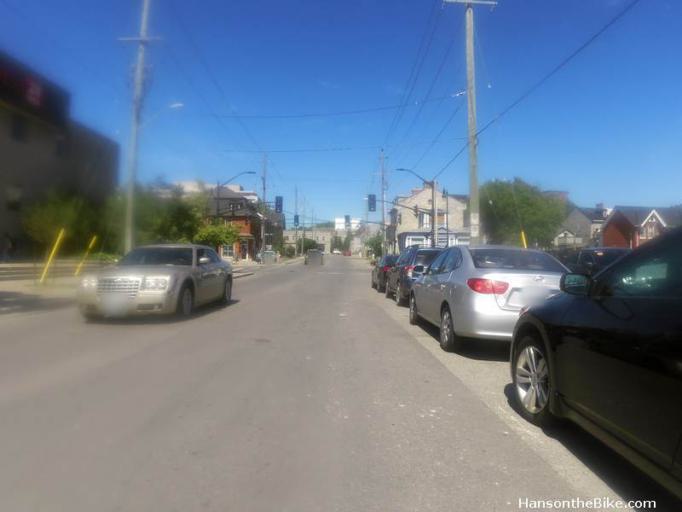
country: CA
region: Ontario
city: Kingston
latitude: 44.2333
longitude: -76.4813
